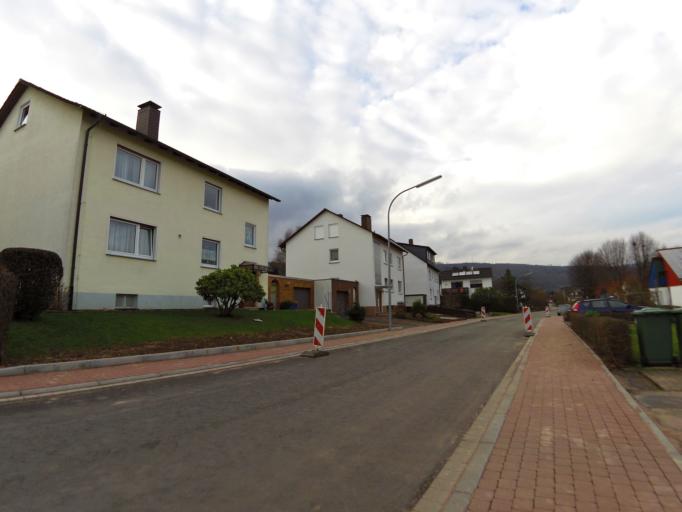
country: DE
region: Lower Saxony
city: Buhren
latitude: 51.4772
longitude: 9.6145
